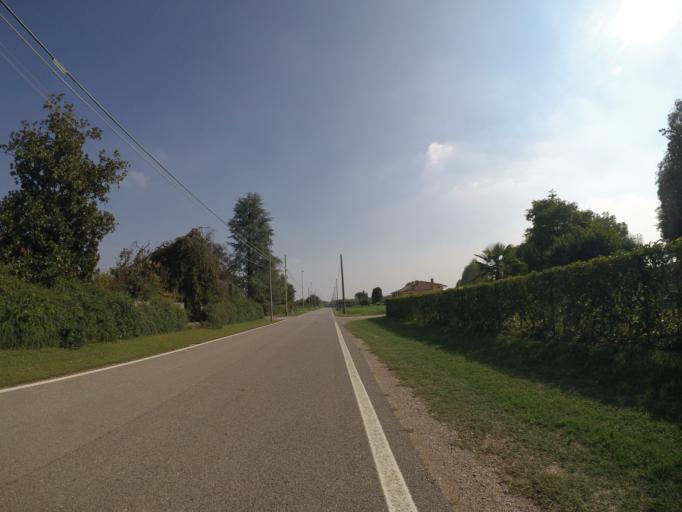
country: IT
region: Friuli Venezia Giulia
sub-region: Provincia di Udine
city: Basiliano
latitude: 45.9890
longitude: 13.0313
